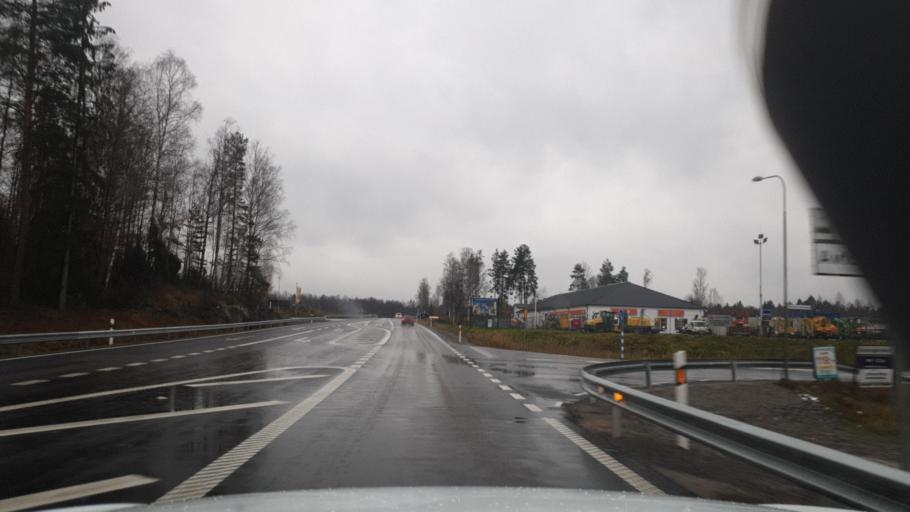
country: SE
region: Vaermland
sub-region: Arvika Kommun
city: Arvika
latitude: 59.6781
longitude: 12.5938
